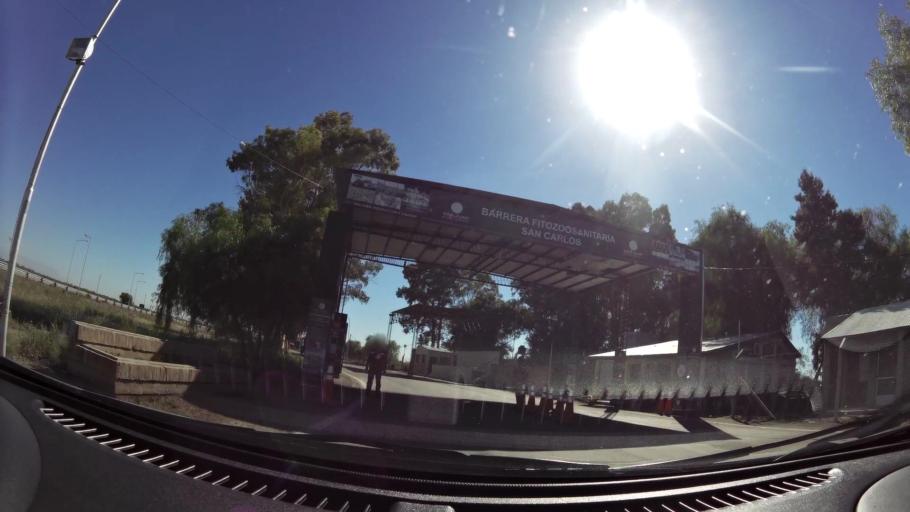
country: AR
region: San Juan
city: Villa Media Agua
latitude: -32.2504
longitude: -68.5073
